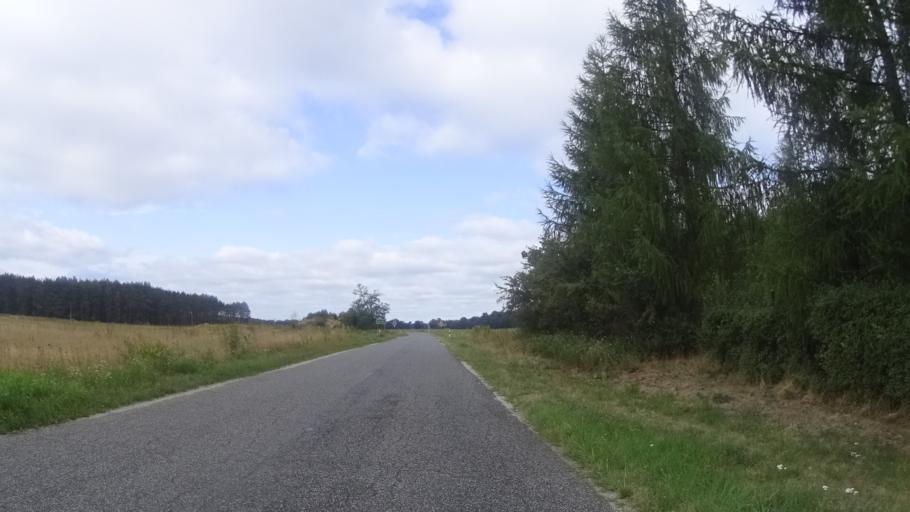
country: PL
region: Lubusz
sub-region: Powiat zarski
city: Przewoz
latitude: 51.4796
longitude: 14.9411
